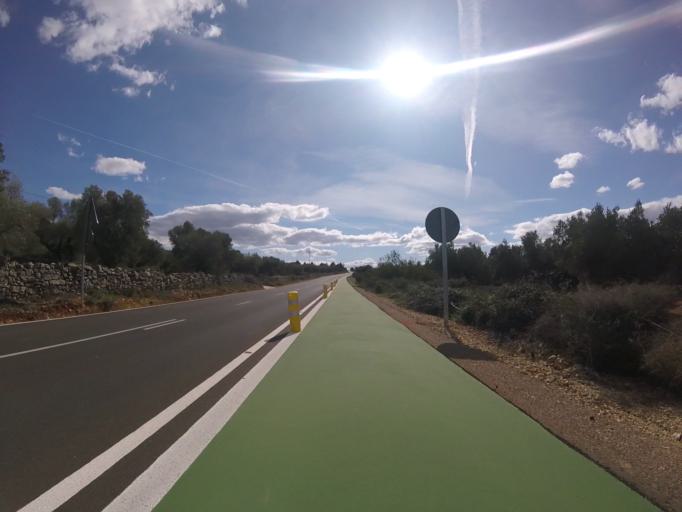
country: ES
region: Valencia
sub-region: Provincia de Castello
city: Albocasser
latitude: 40.4144
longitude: 0.0710
